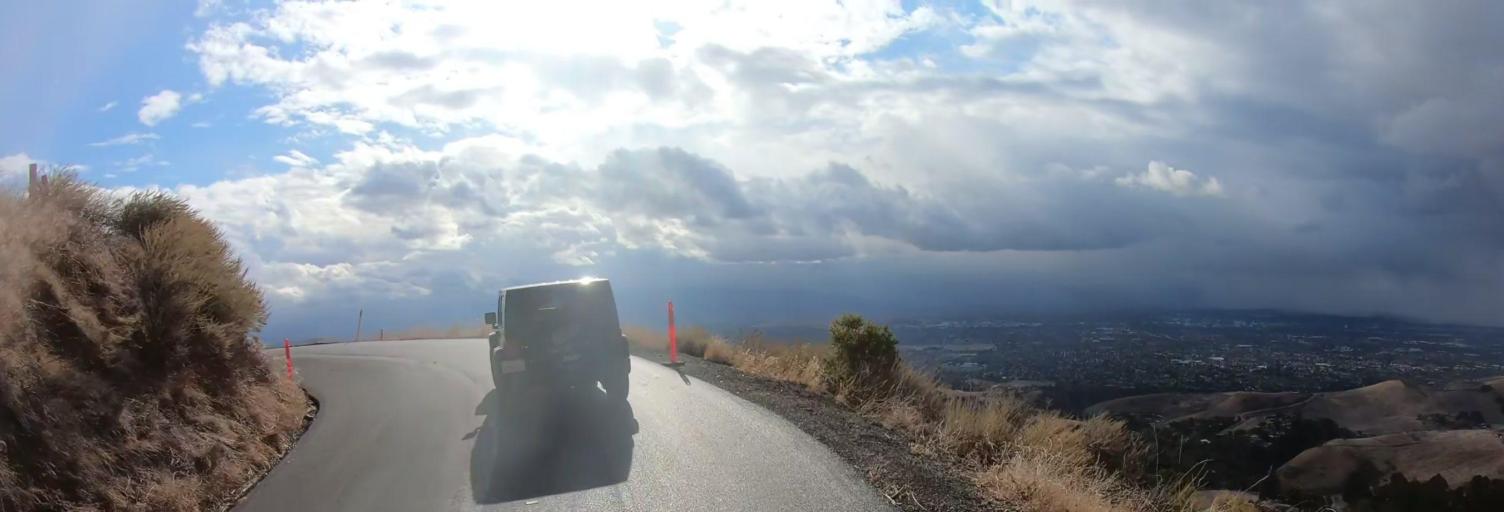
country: US
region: California
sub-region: Santa Clara County
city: East Foothills
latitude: 37.3715
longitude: -121.7695
